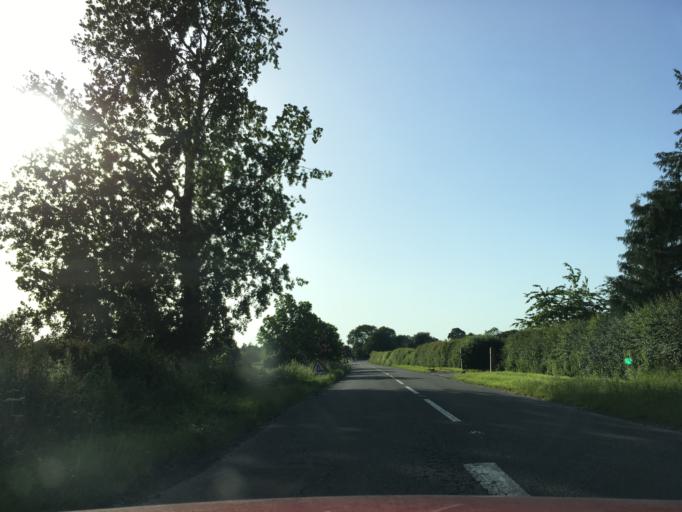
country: GB
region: England
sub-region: Wiltshire
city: Cricklade
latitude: 51.7115
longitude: -1.8883
